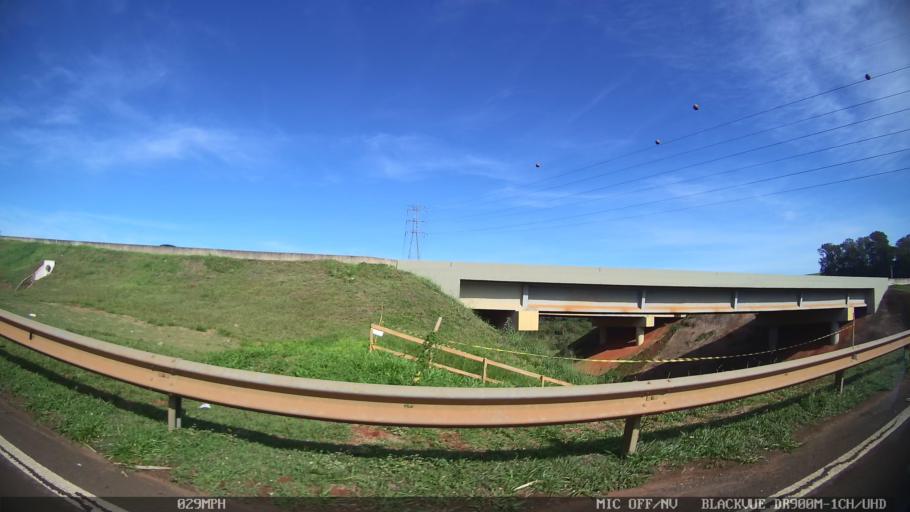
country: BR
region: Sao Paulo
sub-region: Araras
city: Araras
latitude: -22.3953
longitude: -47.3907
